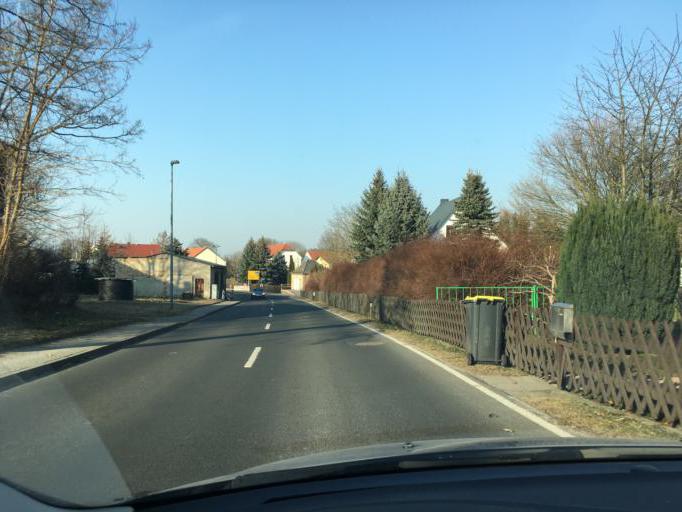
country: DE
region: Saxony
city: Kitzscher
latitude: 51.1213
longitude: 12.5898
